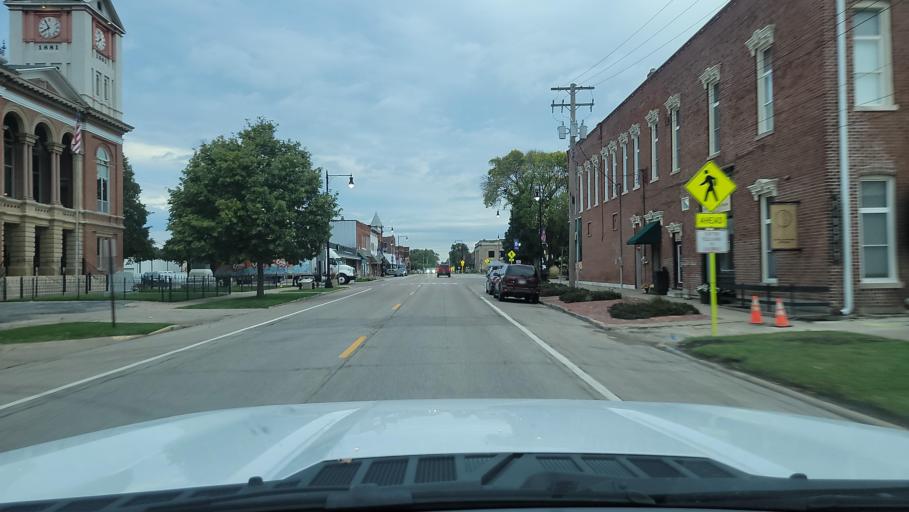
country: US
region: Illinois
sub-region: Schuyler County
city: Rushville
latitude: 40.1200
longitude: -90.5636
